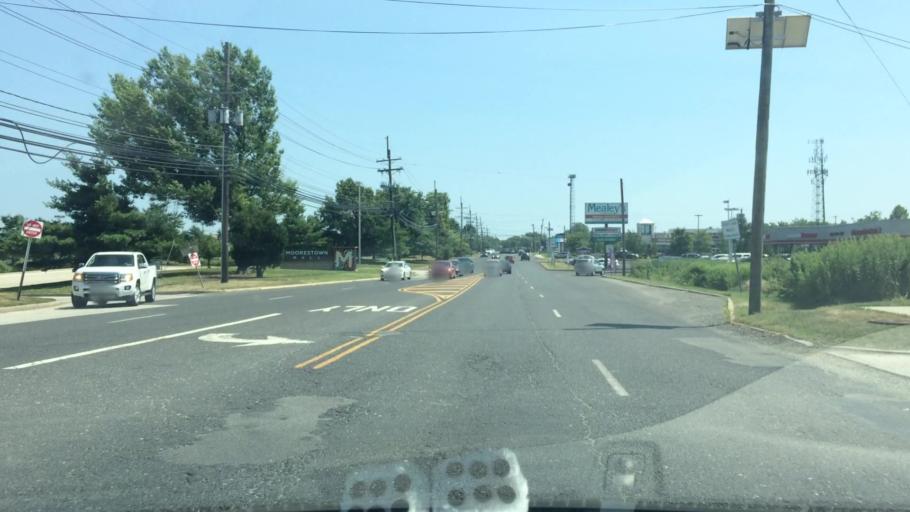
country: US
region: New Jersey
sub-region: Burlington County
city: Moorestown-Lenola
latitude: 39.9430
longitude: -74.9680
